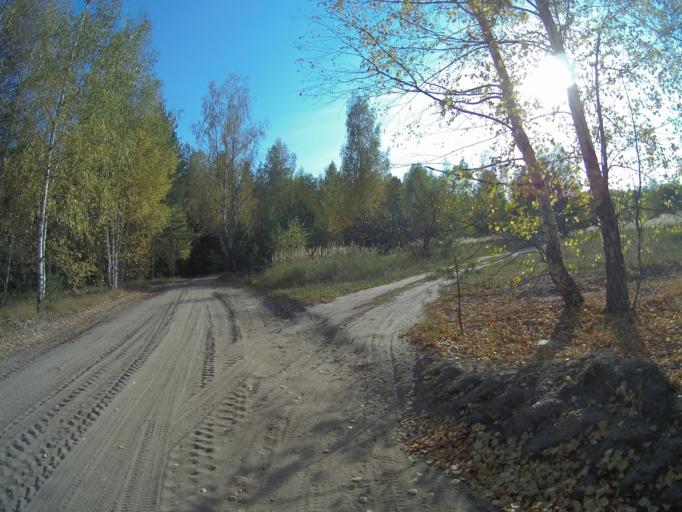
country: RU
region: Vladimir
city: Urshel'skiy
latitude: 55.8249
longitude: 40.1613
